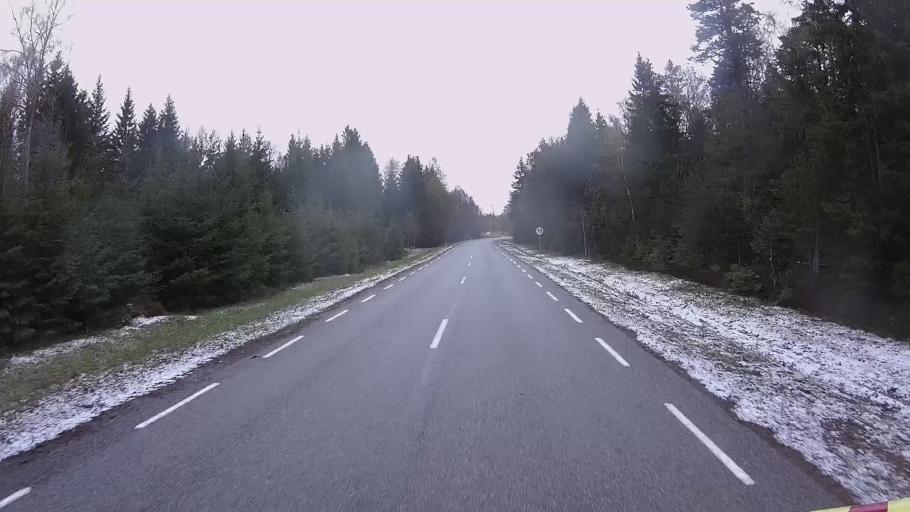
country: EE
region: Hiiumaa
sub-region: Kaerdla linn
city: Kardla
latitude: 59.0667
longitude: 22.6872
